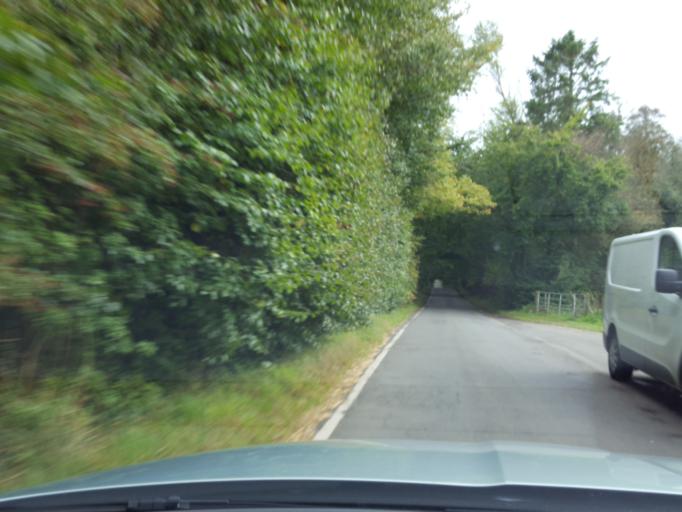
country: GB
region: Scotland
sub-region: West Lothian
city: Broxburn
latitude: 55.9161
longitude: -3.4594
